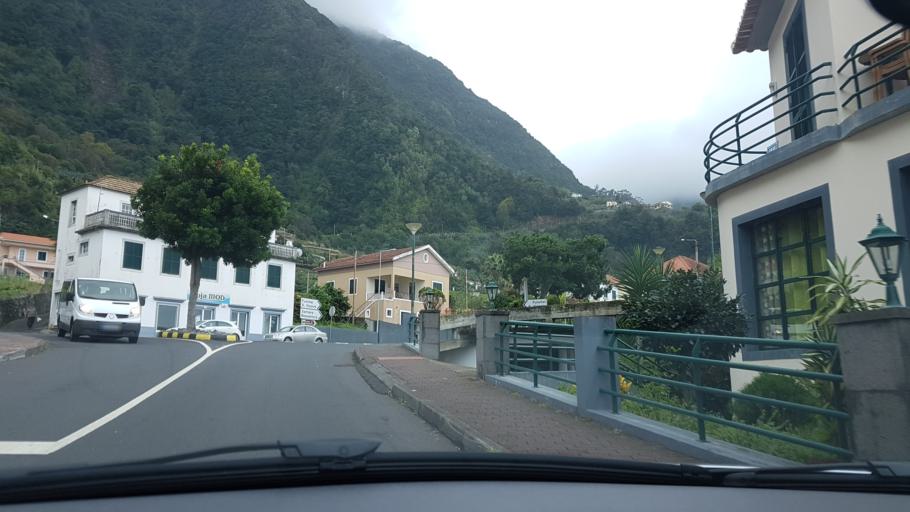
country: PT
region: Madeira
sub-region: Sao Vicente
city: Sao Vicente
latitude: 32.8232
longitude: -16.9895
